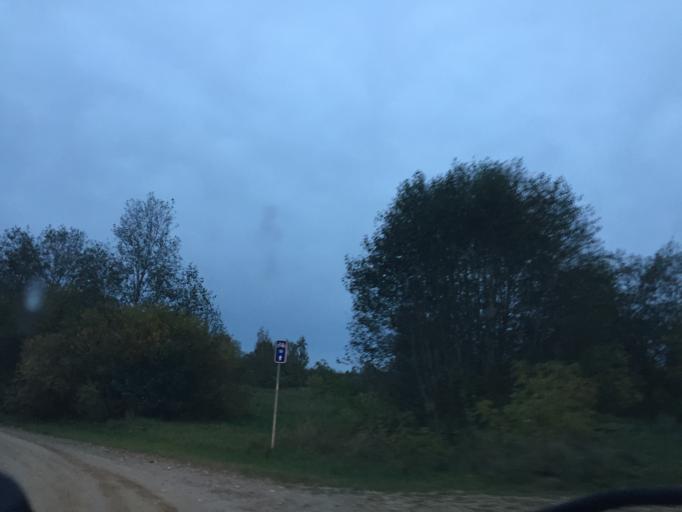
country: LV
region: Adazi
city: Adazi
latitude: 57.0796
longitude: 24.3706
